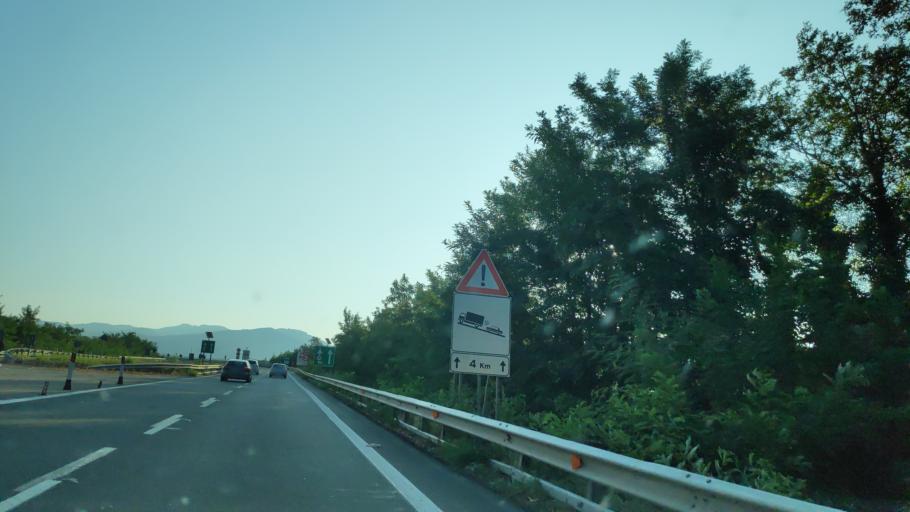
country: IT
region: Calabria
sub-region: Provincia di Cosenza
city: Carpanzano
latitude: 39.1459
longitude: 16.2791
